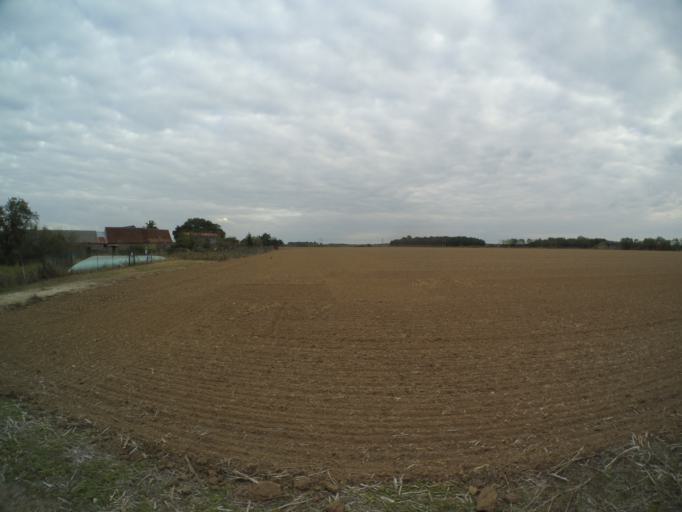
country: FR
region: Centre
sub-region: Departement d'Indre-et-Loire
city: Reugny
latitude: 47.4804
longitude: 0.9252
